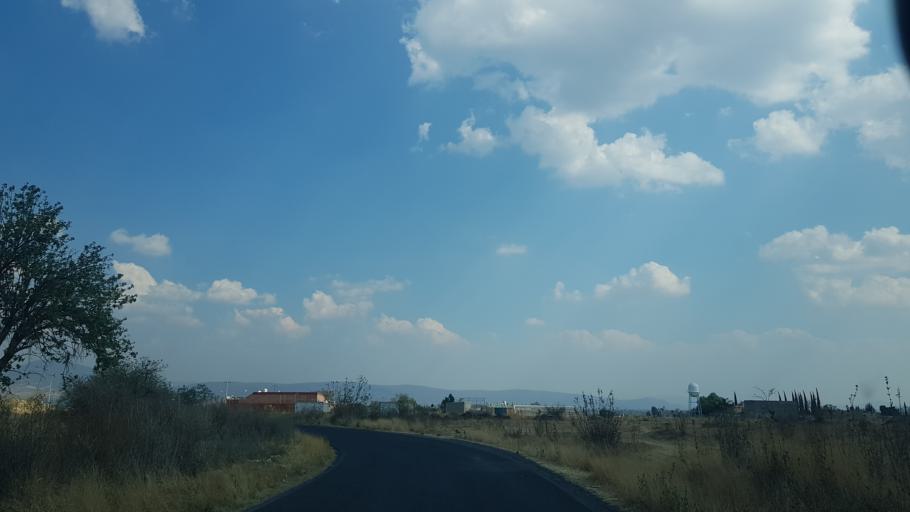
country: MX
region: Puebla
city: Atlixco
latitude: 18.9188
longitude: -98.4818
